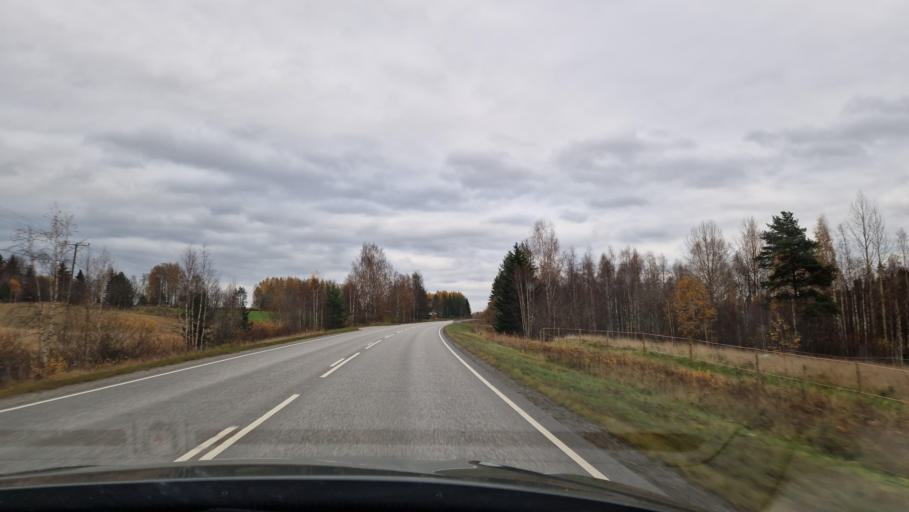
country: FI
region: North Karelia
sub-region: Pielisen Karjala
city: Valtimo
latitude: 63.5295
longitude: 28.9018
